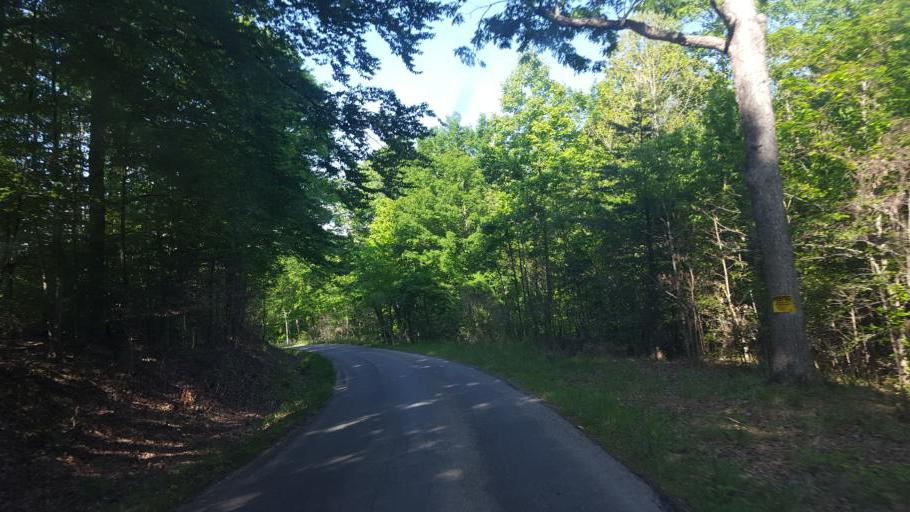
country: US
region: Ohio
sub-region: Jackson County
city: Wellston
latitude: 38.9965
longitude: -82.3983
